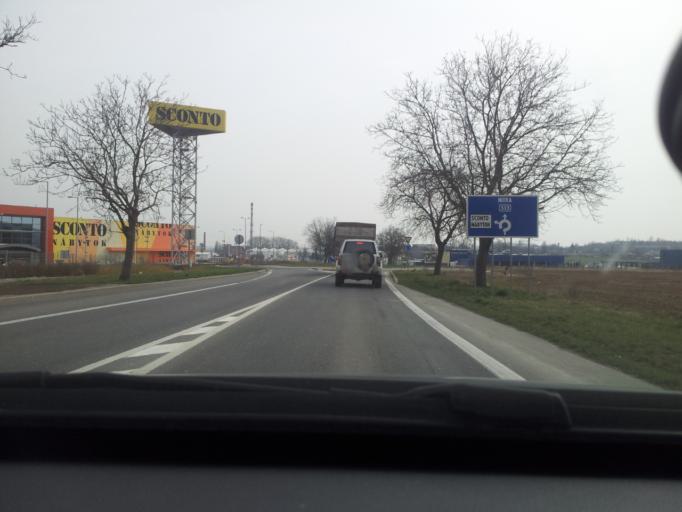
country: SK
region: Nitriansky
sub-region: Okres Nitra
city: Nitra
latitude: 48.3244
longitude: 18.0329
